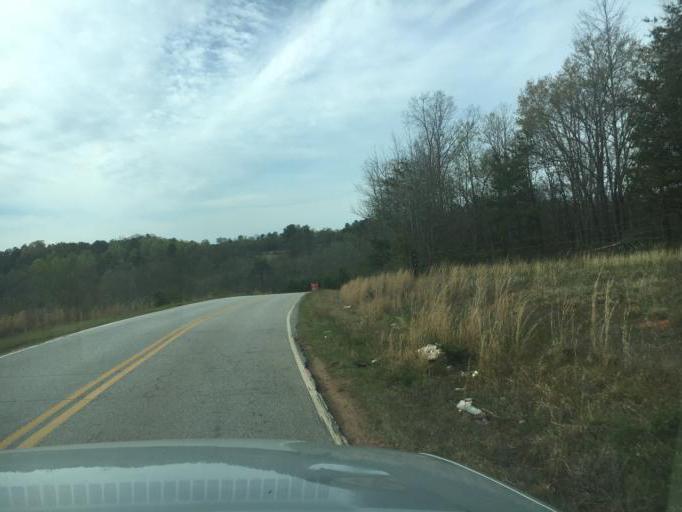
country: US
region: South Carolina
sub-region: Spartanburg County
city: Duncan
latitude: 34.9301
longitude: -82.1662
